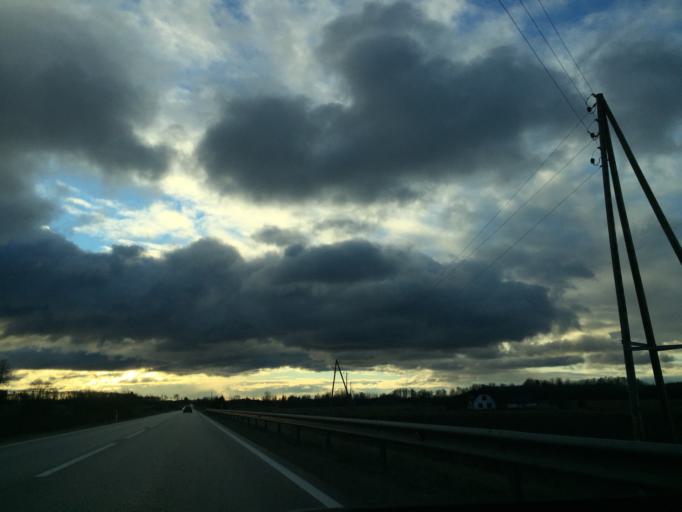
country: LV
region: Sigulda
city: Sigulda
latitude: 57.2543
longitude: 24.8593
